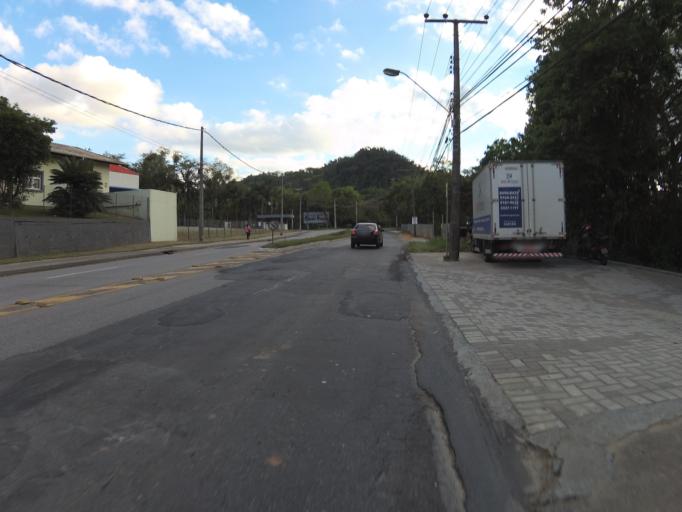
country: BR
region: Santa Catarina
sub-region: Blumenau
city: Blumenau
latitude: -26.8904
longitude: -49.1219
